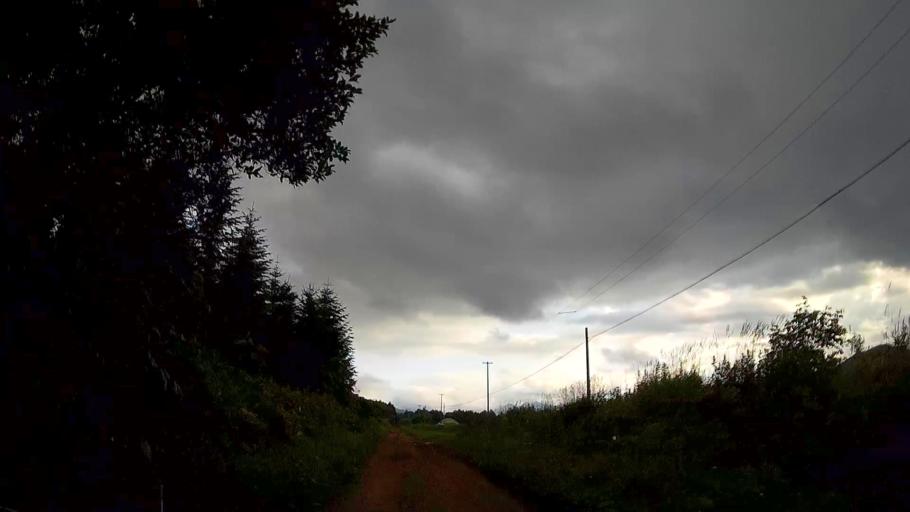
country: JP
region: Hokkaido
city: Nanae
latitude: 42.1232
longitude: 140.4077
